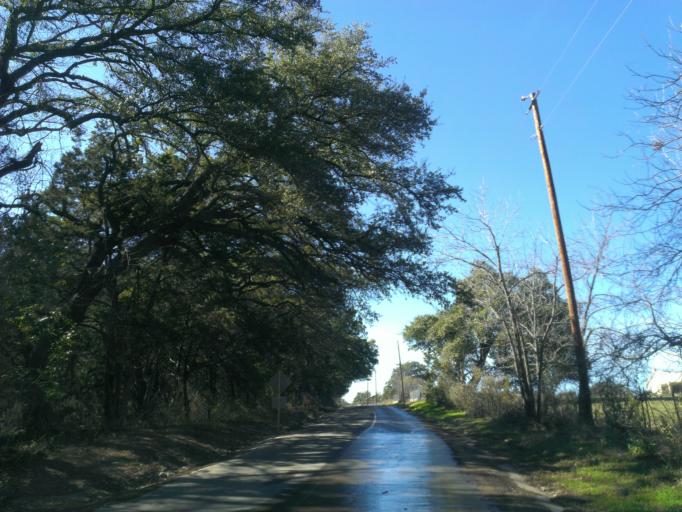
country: US
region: Texas
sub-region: Travis County
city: Briarcliff
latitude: 30.4768
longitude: -98.1531
